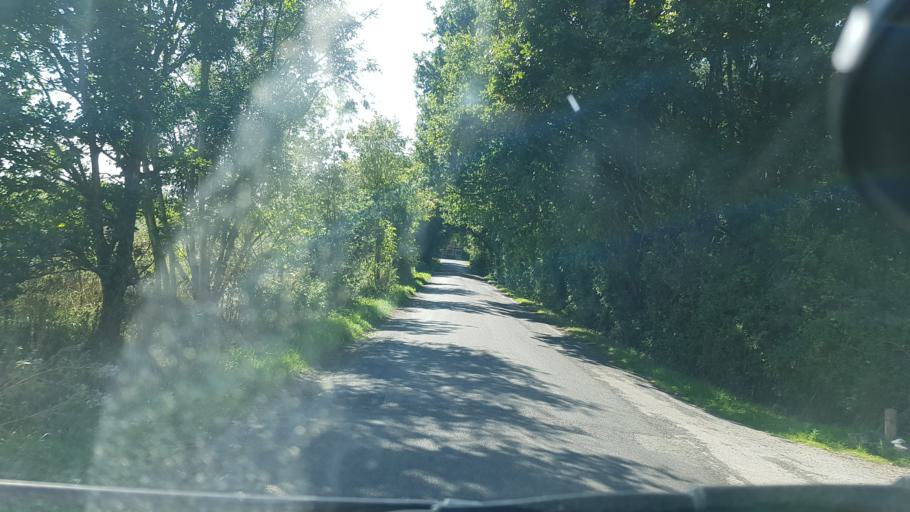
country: GB
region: England
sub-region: Surrey
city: Cranleigh
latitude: 51.1635
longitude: -0.4999
